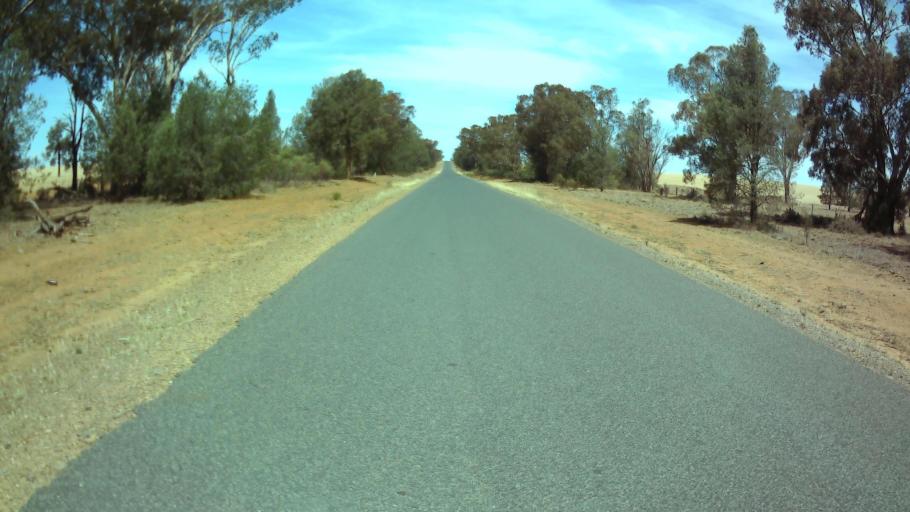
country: AU
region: New South Wales
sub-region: Weddin
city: Grenfell
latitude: -33.8958
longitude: 147.7496
